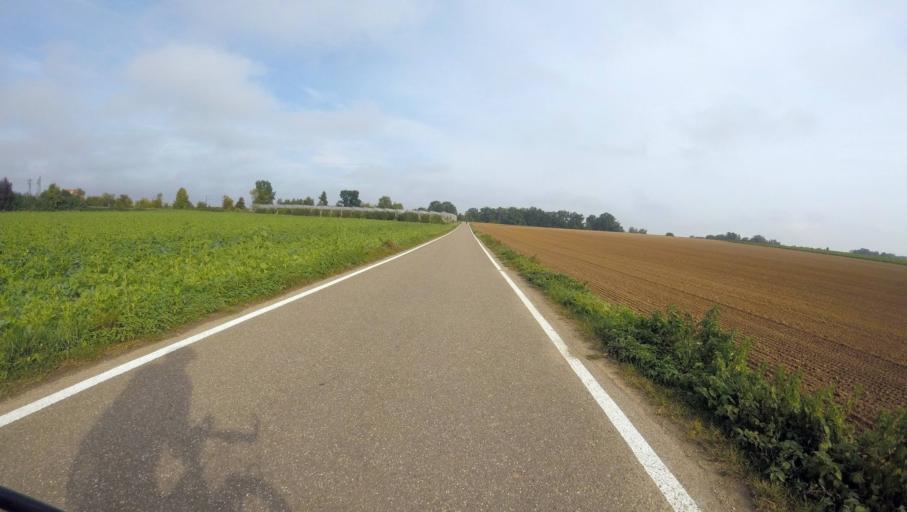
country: DE
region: Baden-Wuerttemberg
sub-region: Regierungsbezirk Stuttgart
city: Bondorf
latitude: 48.5291
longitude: 8.8289
